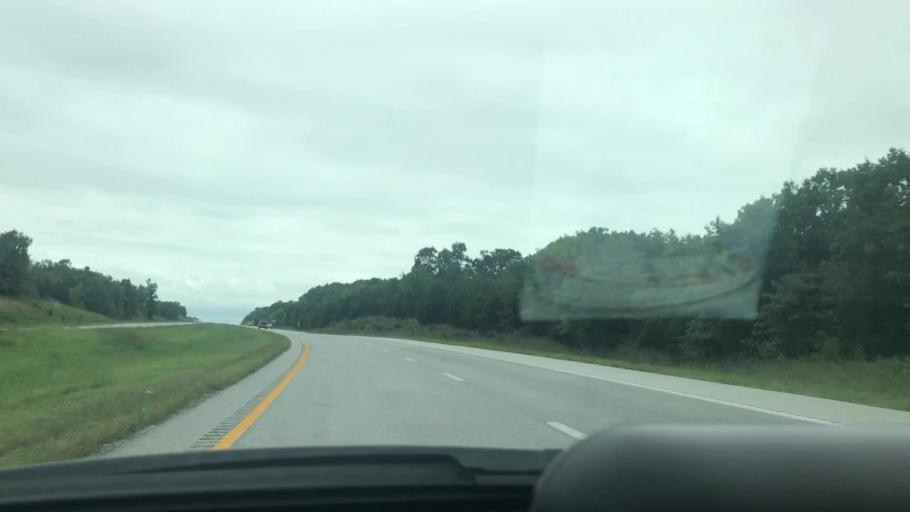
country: US
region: Missouri
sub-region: Greene County
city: Fair Grove
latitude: 37.3206
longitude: -93.1680
